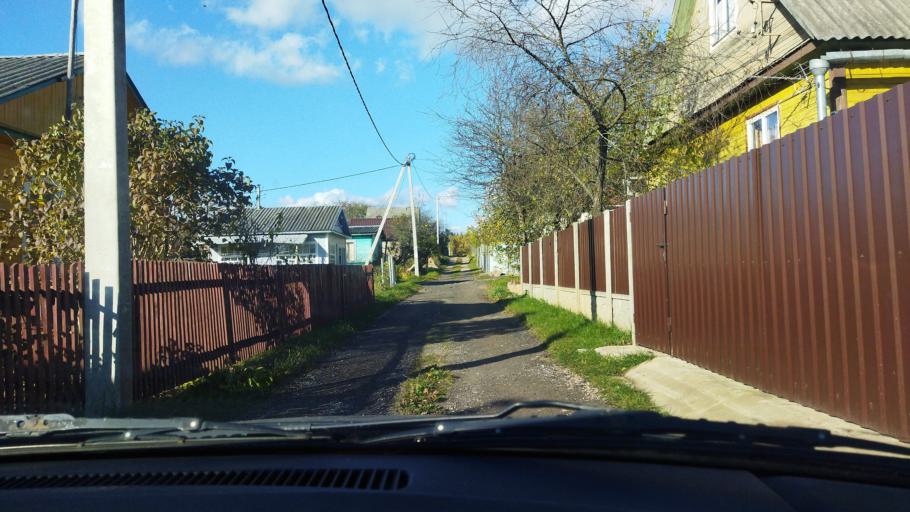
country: BY
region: Minsk
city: Slabada
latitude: 53.9888
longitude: 27.8933
